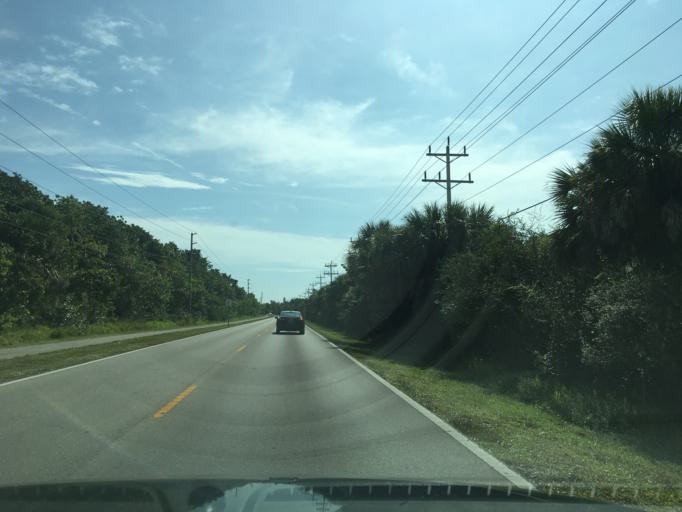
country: US
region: Florida
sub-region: Lee County
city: Saint James City
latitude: 26.4595
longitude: -82.1458
